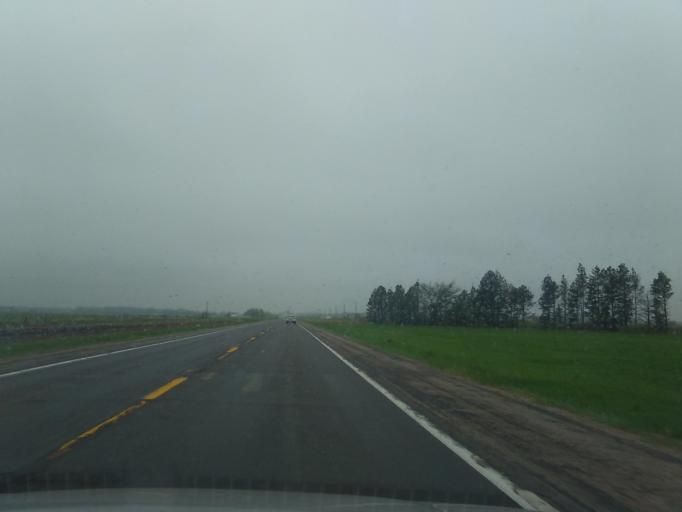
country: US
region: Nebraska
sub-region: Cuming County
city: West Point
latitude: 41.9153
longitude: -96.7888
